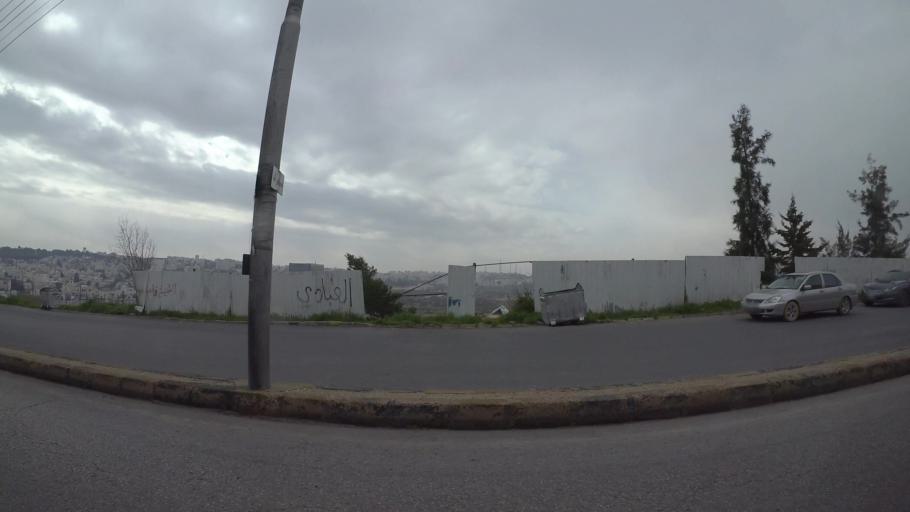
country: JO
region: Amman
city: Umm as Summaq
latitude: 31.9027
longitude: 35.8504
